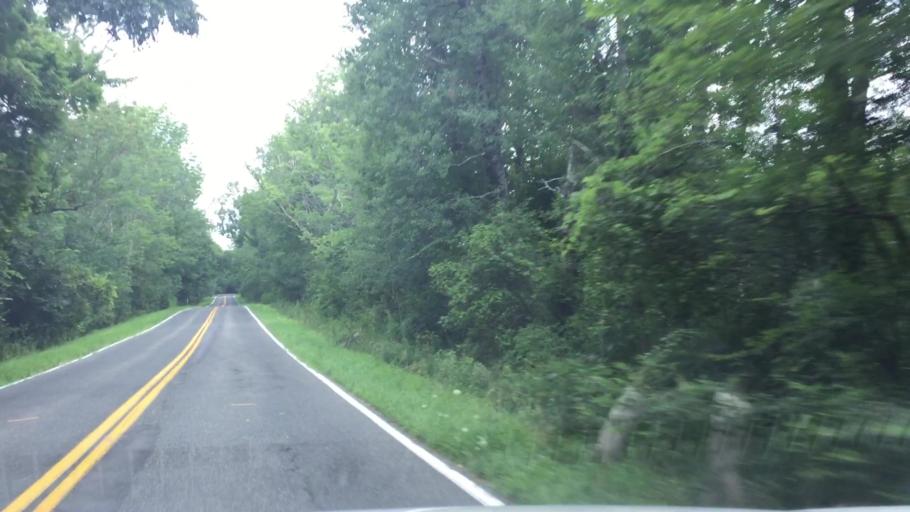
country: US
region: Massachusetts
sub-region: Berkshire County
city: Housatonic
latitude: 42.2779
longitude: -73.4081
